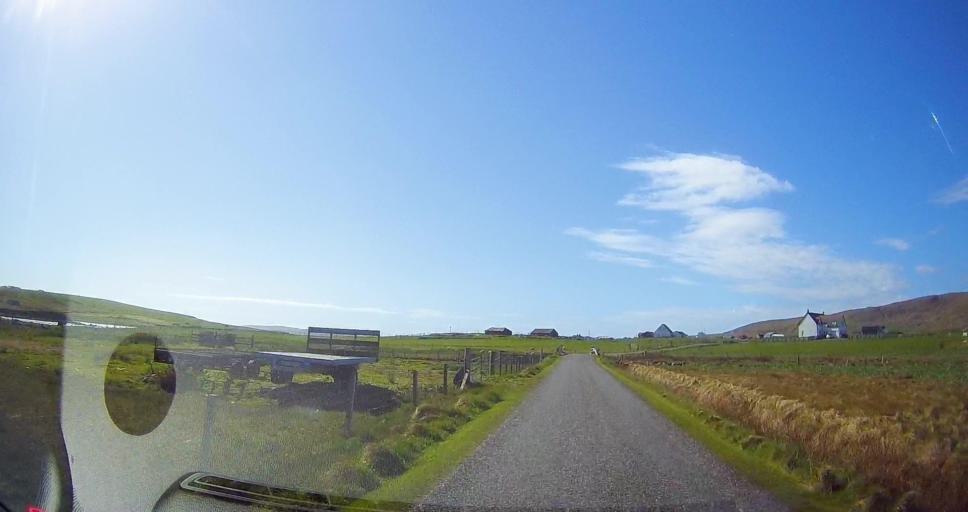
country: GB
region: Scotland
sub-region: Shetland Islands
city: Sandwick
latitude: 60.0437
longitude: -1.2169
